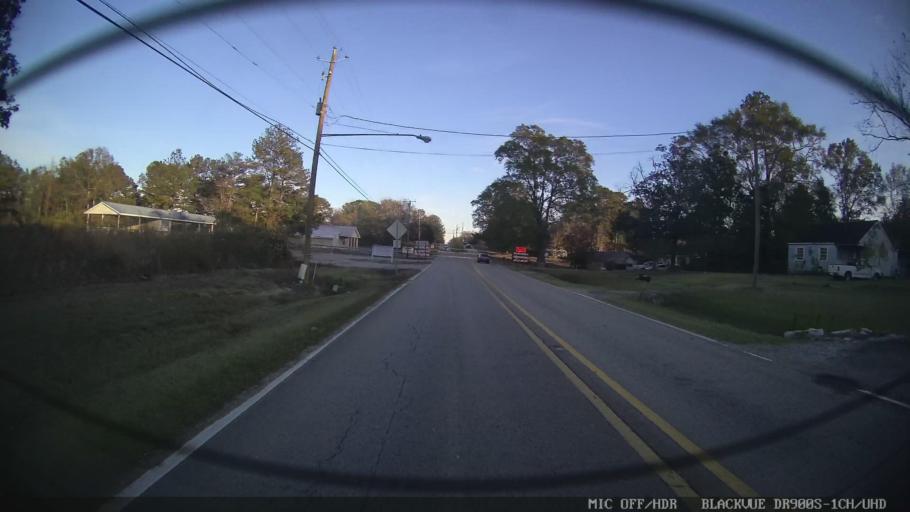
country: US
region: Mississippi
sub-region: Lamar County
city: Lumberton
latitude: 31.0066
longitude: -89.4661
